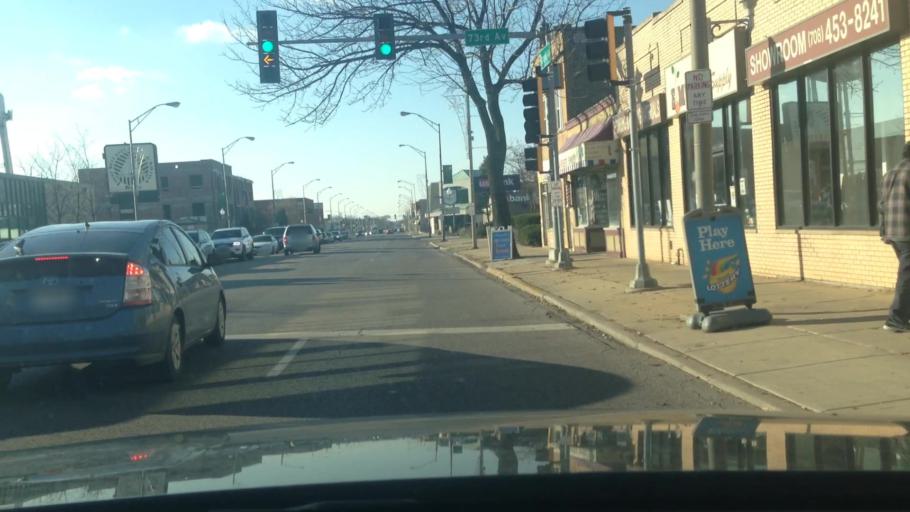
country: US
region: Illinois
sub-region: Cook County
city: Elmwood Park
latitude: 41.9245
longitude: -87.8088
